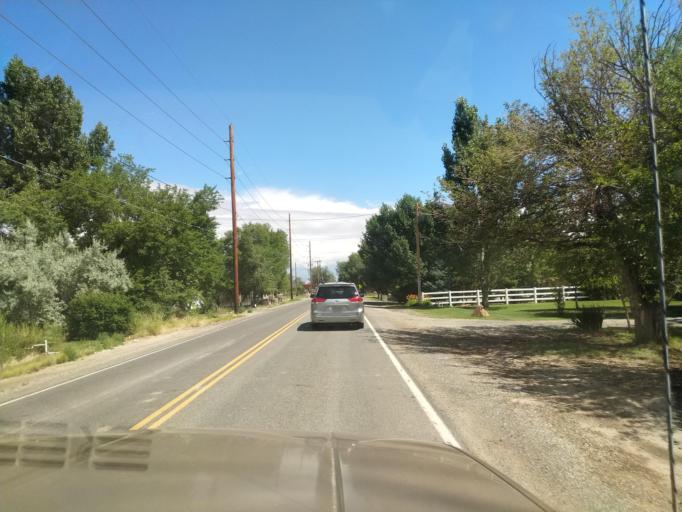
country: US
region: Colorado
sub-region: Mesa County
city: Redlands
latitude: 39.1186
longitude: -108.6081
